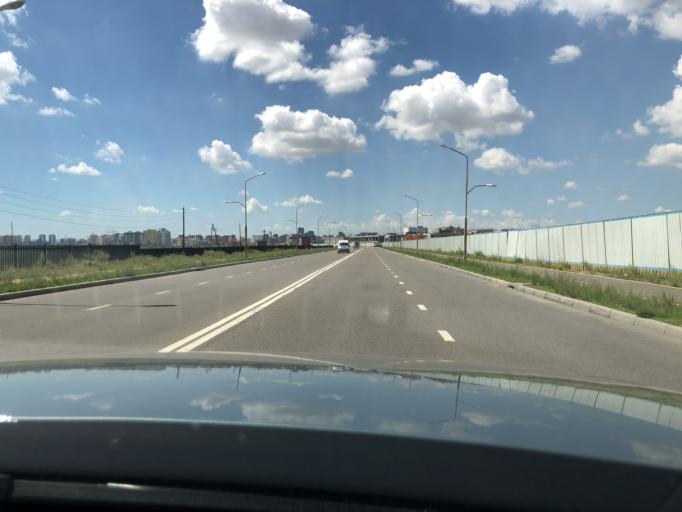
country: MN
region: Ulaanbaatar
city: Ulaanbaatar
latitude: 47.9044
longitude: 106.9753
